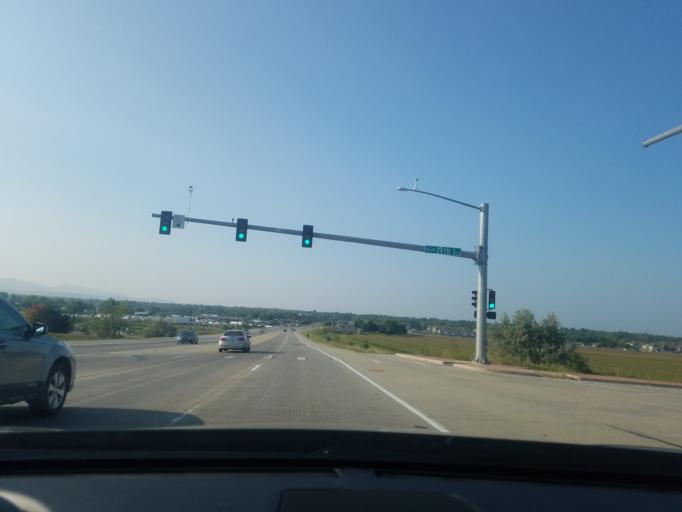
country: US
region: Colorado
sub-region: Larimer County
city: Campion
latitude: 40.3726
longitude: -105.0726
